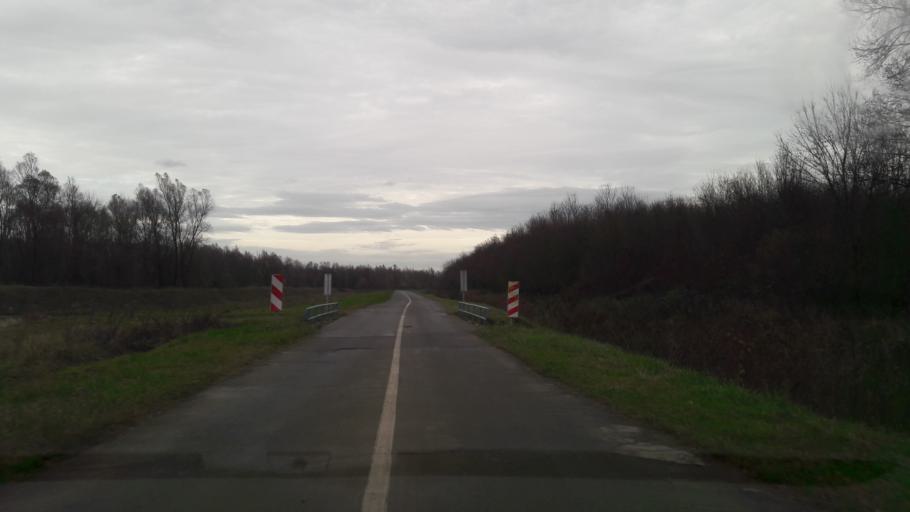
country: HR
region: Osjecko-Baranjska
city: Velimirovac
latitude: 45.6186
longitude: 18.0750
